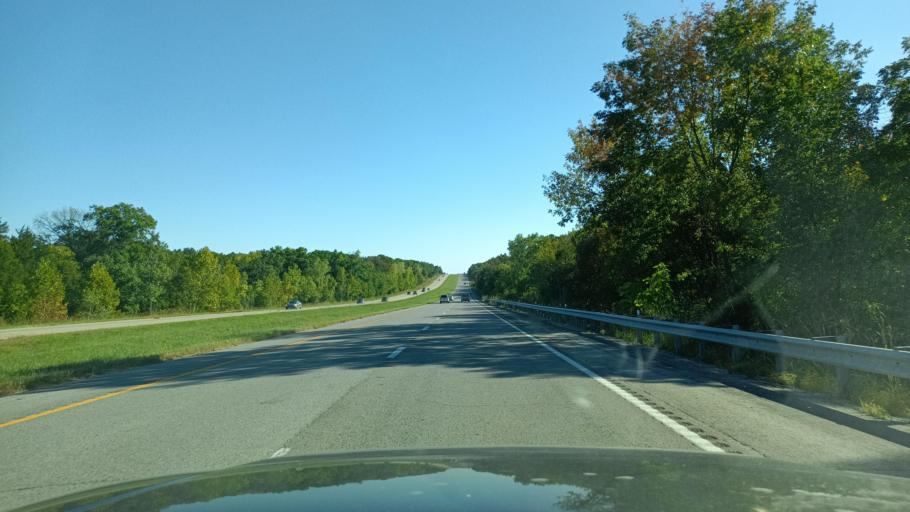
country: US
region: Missouri
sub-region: Boone County
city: Hallsville
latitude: 39.1062
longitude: -92.3293
